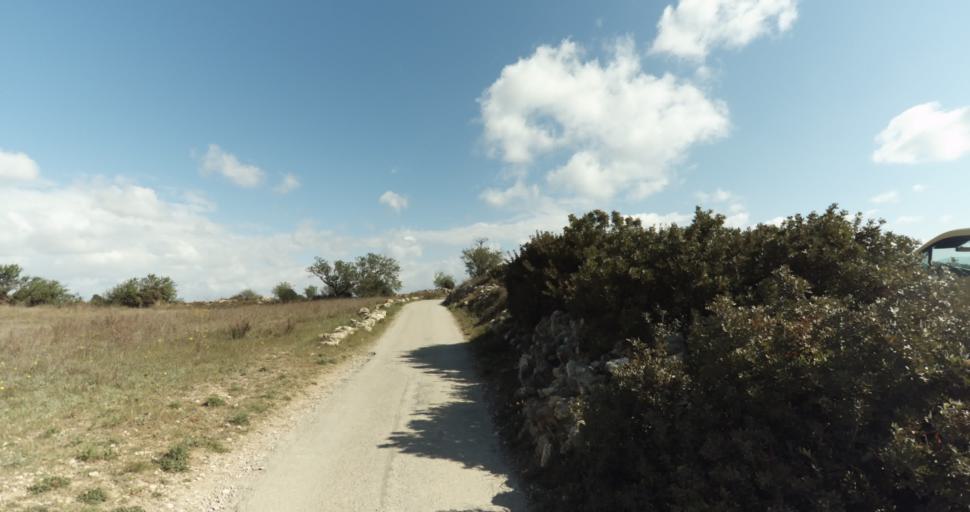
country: FR
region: Languedoc-Roussillon
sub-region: Departement de l'Aude
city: Leucate
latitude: 42.9202
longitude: 3.0366
